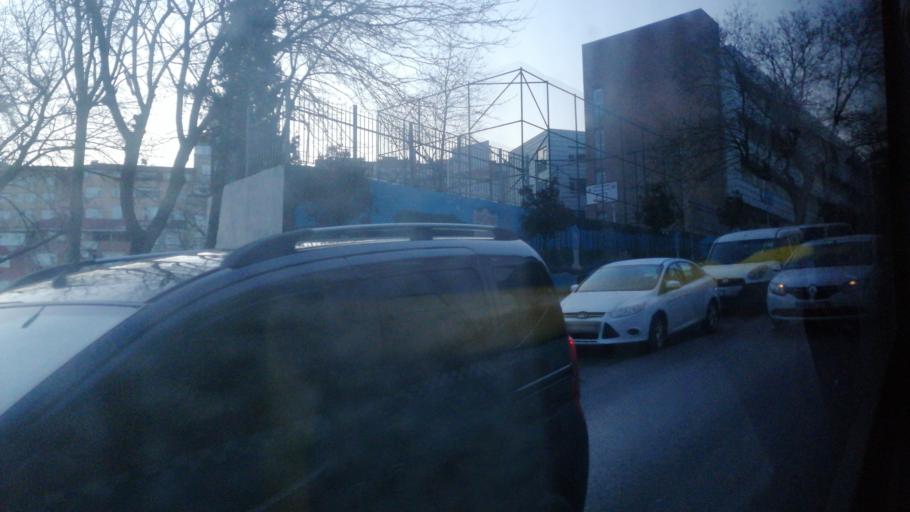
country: TR
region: Istanbul
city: Sisli
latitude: 41.0844
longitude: 28.9885
